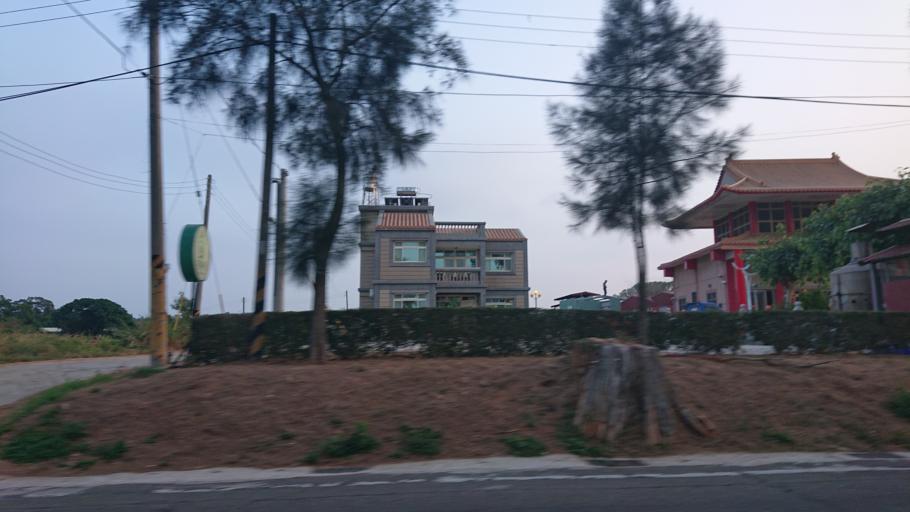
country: TW
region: Fukien
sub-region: Kinmen
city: Jincheng
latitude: 24.4519
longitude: 118.3495
